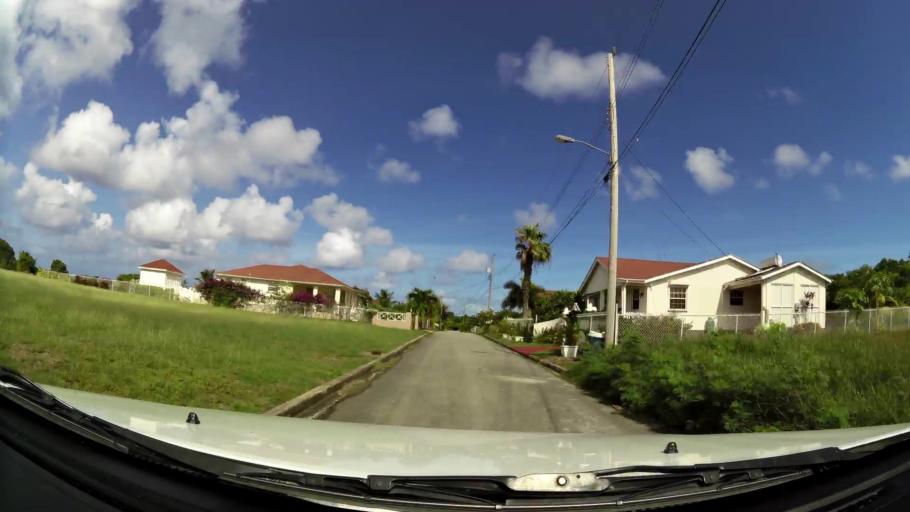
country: BB
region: Saint Lucy
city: Checker Hall
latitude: 13.2722
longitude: -59.6442
